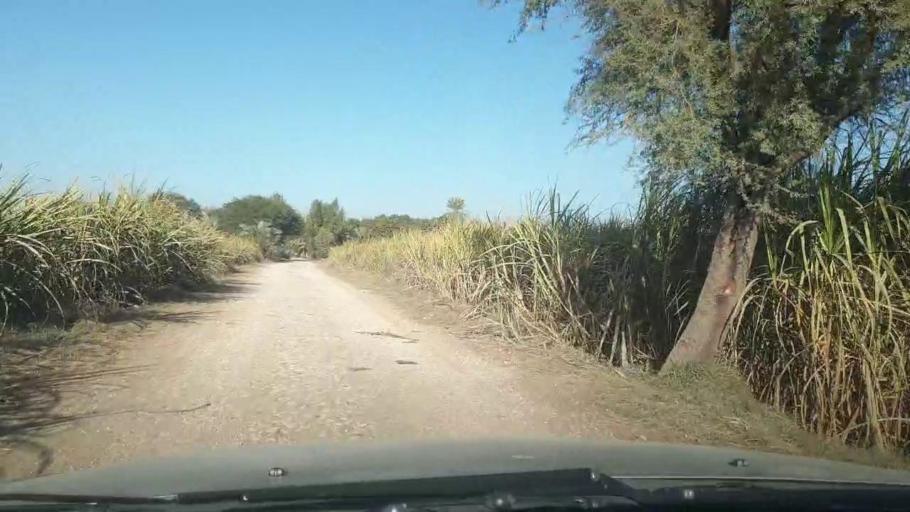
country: PK
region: Sindh
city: Adilpur
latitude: 27.9590
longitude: 69.2017
